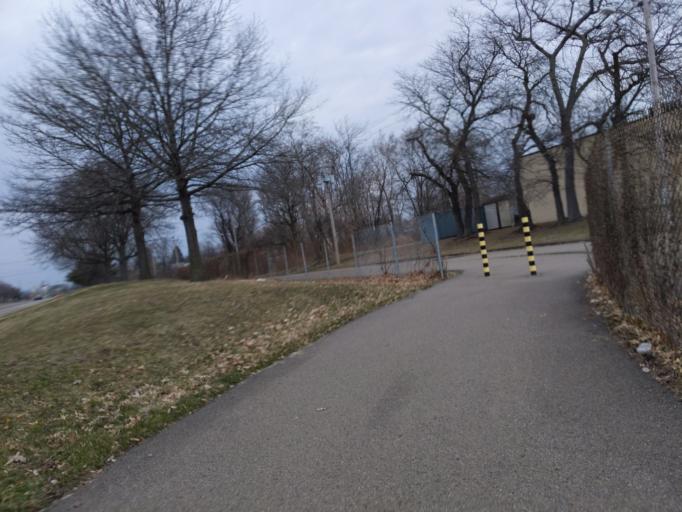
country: US
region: New York
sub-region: Chemung County
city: Elmira
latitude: 42.1065
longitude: -76.8113
